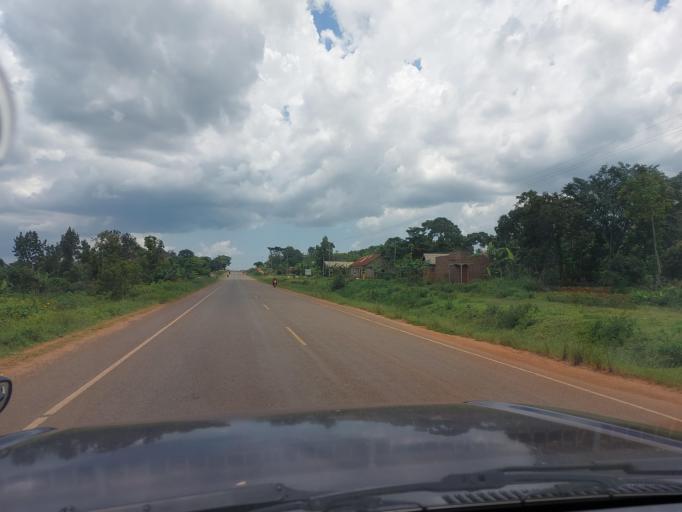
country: UG
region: Central Region
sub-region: Mukono District
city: Mukono
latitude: 0.2897
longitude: 32.7881
